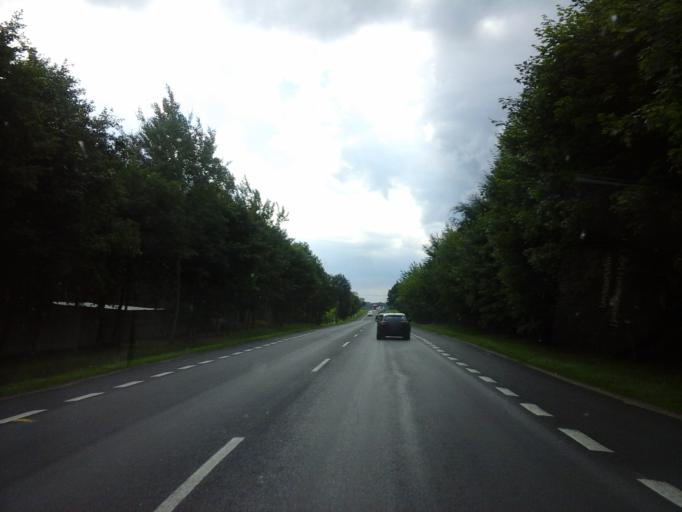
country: PL
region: West Pomeranian Voivodeship
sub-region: Powiat bialogardzki
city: Karlino
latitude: 54.0530
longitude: 15.9143
